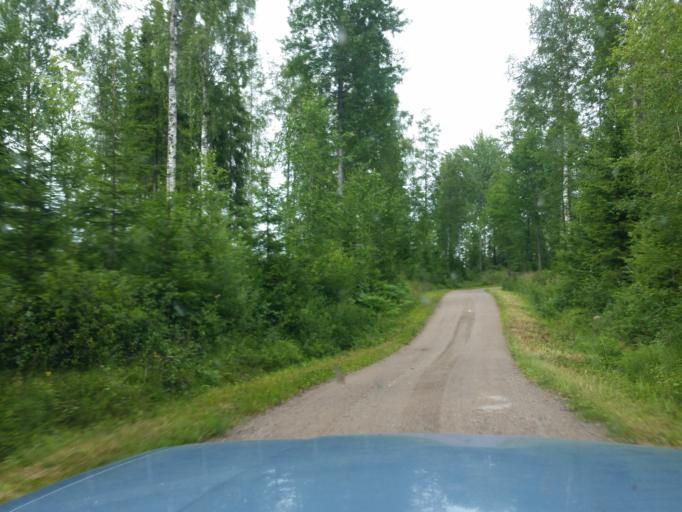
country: FI
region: Uusimaa
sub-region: Helsinki
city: Kaerkoelae
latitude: 60.5729
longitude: 24.0046
